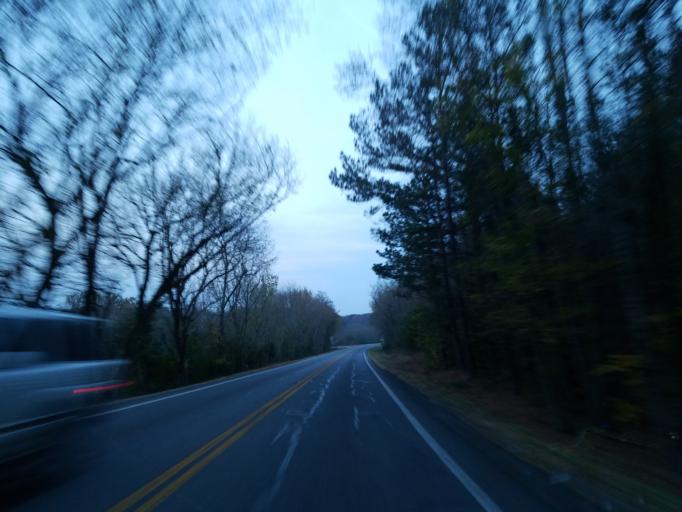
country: US
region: Georgia
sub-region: Pickens County
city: Jasper
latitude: 34.5213
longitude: -84.5257
